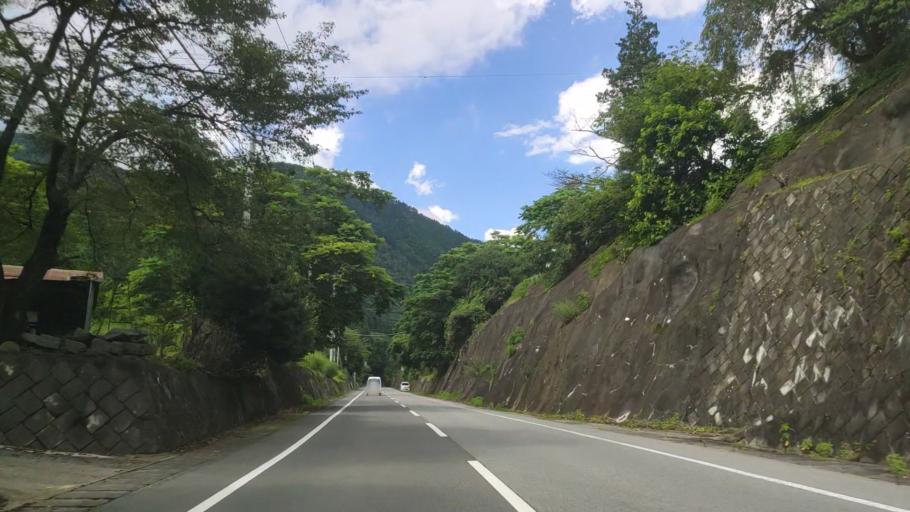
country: JP
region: Yamanashi
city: Enzan
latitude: 35.7917
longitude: 138.7390
